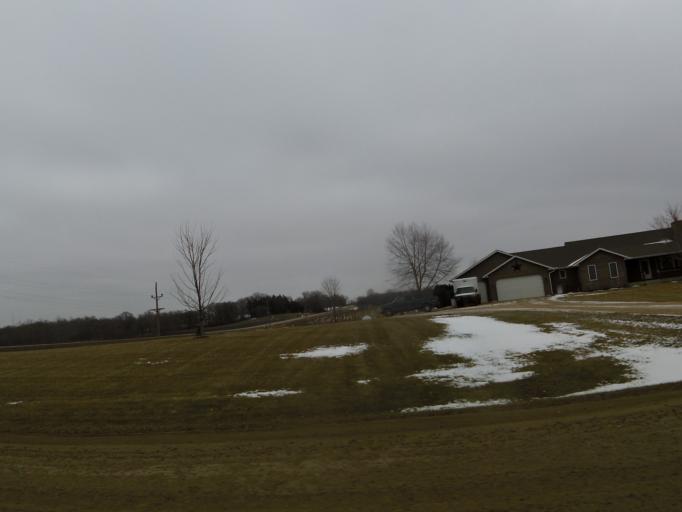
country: US
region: Minnesota
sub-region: Wright County
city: Montrose
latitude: 45.0354
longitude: -93.8583
